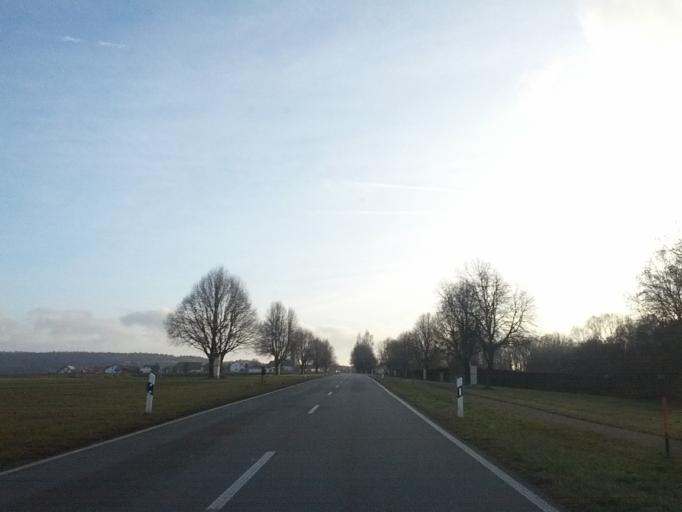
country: DE
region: Baden-Wuerttemberg
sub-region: Tuebingen Region
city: Steinhausen an der Rottum
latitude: 48.0318
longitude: 9.9555
